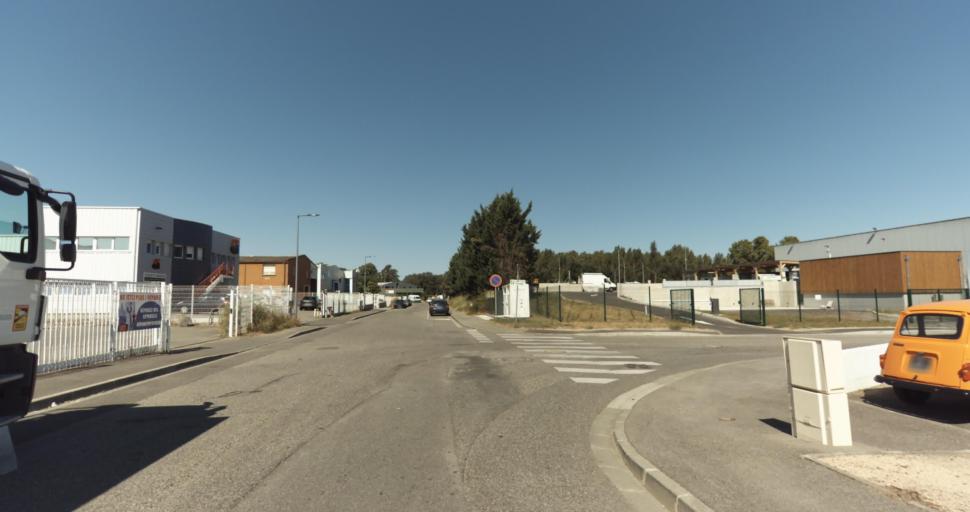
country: FR
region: Midi-Pyrenees
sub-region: Departement de la Haute-Garonne
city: Saint-Jean
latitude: 43.6415
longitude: 1.5011
